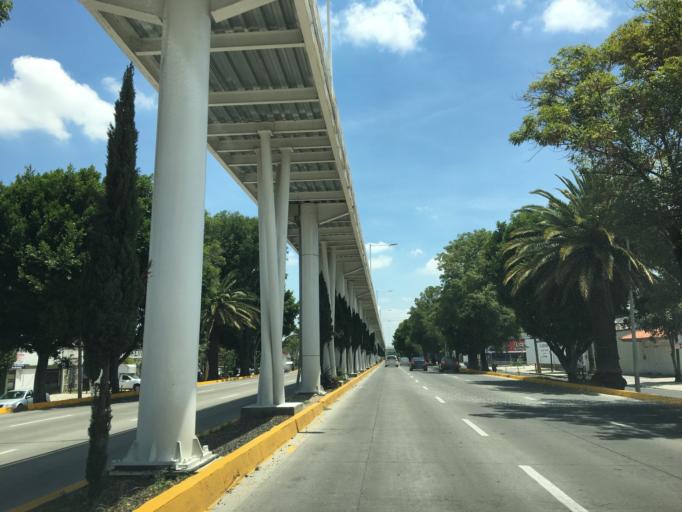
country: MX
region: Puebla
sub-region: Cuautlancingo
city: Sanctorum
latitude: 19.0863
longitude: -98.2290
